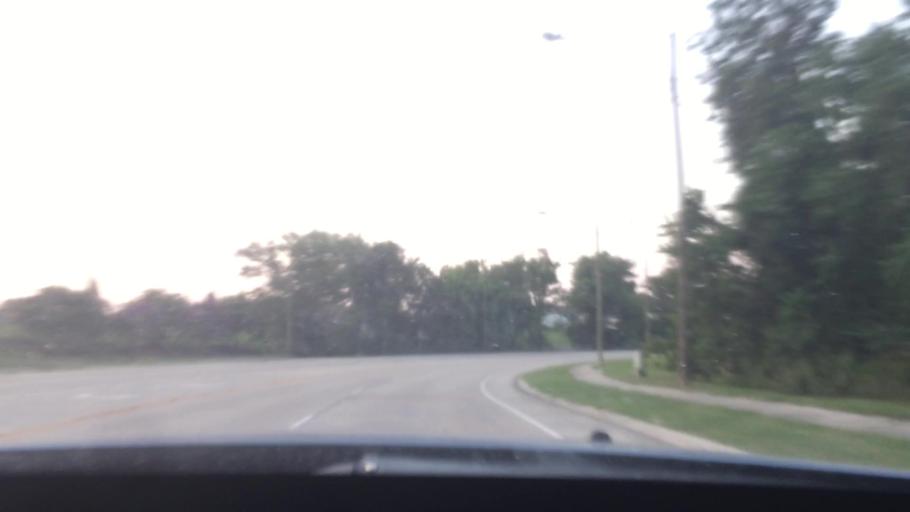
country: US
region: Louisiana
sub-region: East Baton Rouge Parish
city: Westminster
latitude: 30.4290
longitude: -91.0553
